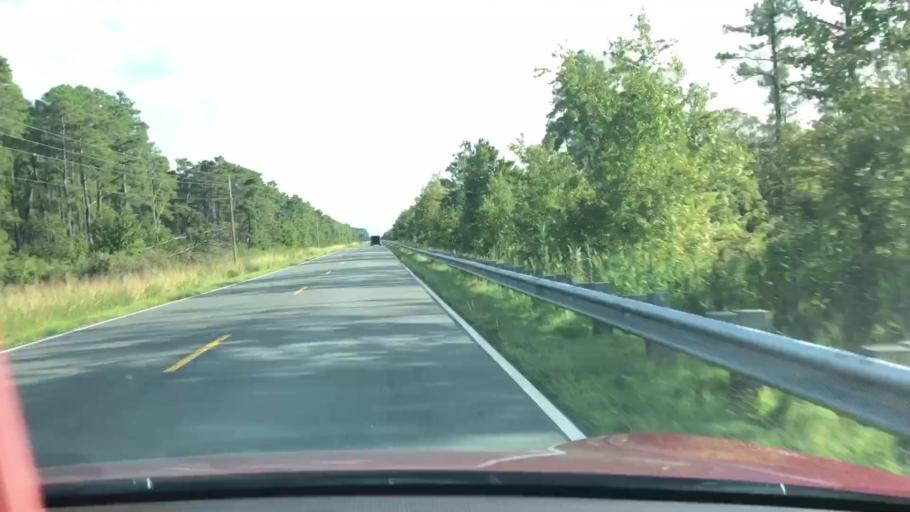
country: US
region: North Carolina
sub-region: Dare County
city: Wanchese
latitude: 35.7829
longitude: -75.7695
